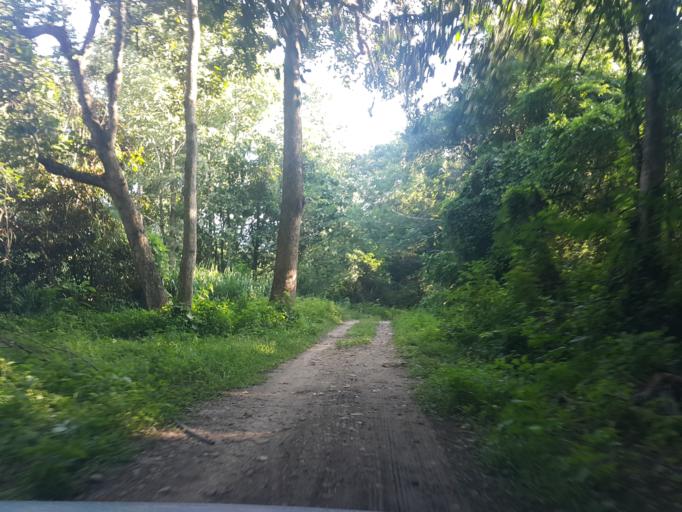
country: TH
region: Chiang Mai
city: Mae On
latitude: 18.7084
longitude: 99.2035
